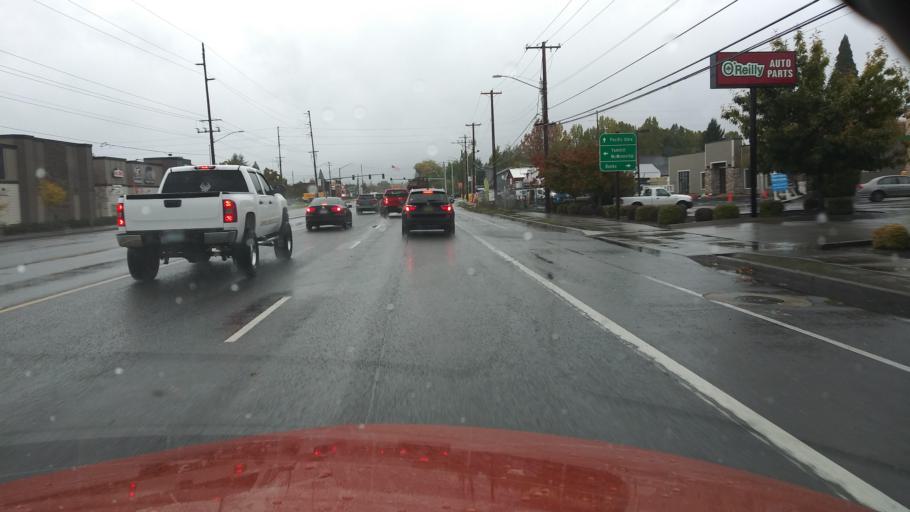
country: US
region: Oregon
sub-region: Washington County
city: Cornelius
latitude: 45.5203
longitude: -123.0815
